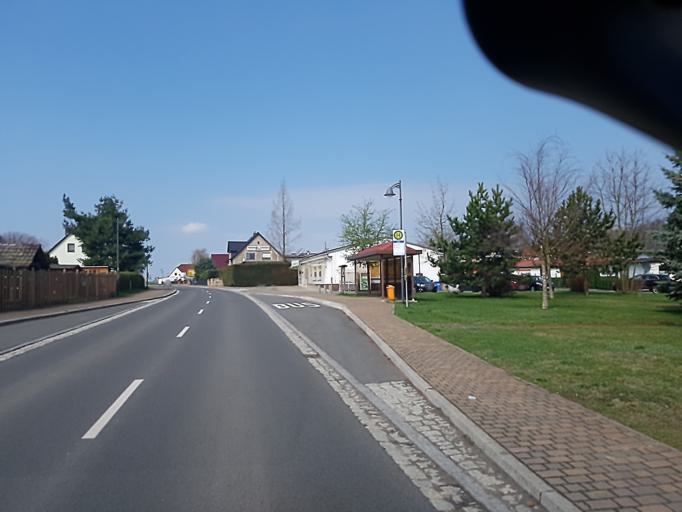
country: DE
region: Saxony
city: Zinna
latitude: 51.5638
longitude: 12.9256
